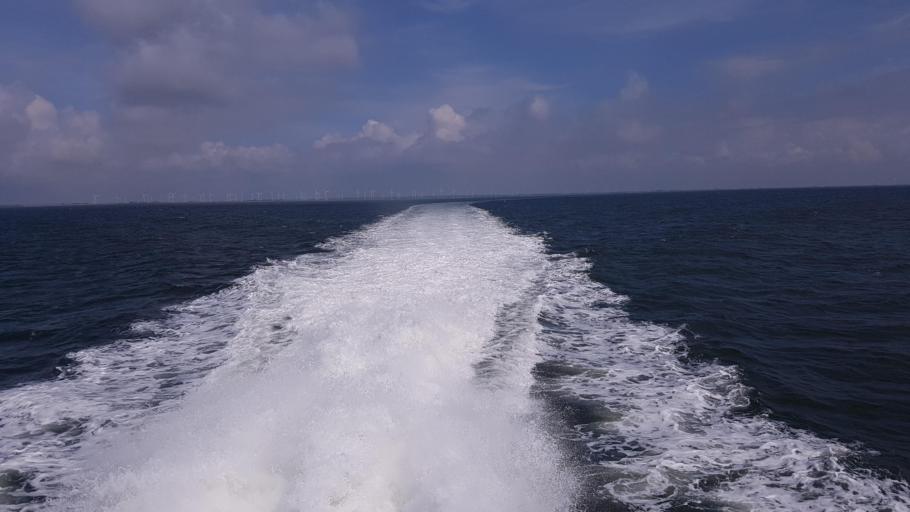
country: DE
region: Schleswig-Holstein
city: Grode
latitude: 54.6213
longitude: 8.7442
